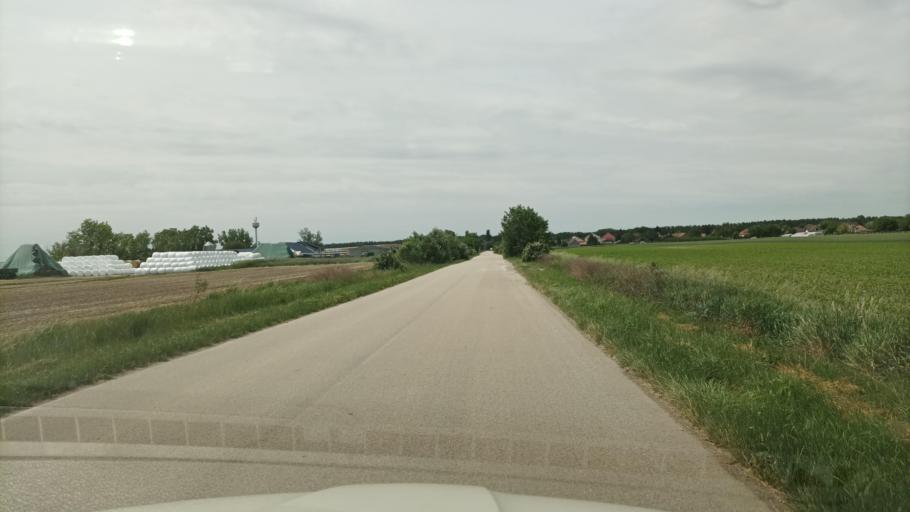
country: HU
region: Fejer
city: Adony
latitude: 47.1175
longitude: 18.9066
